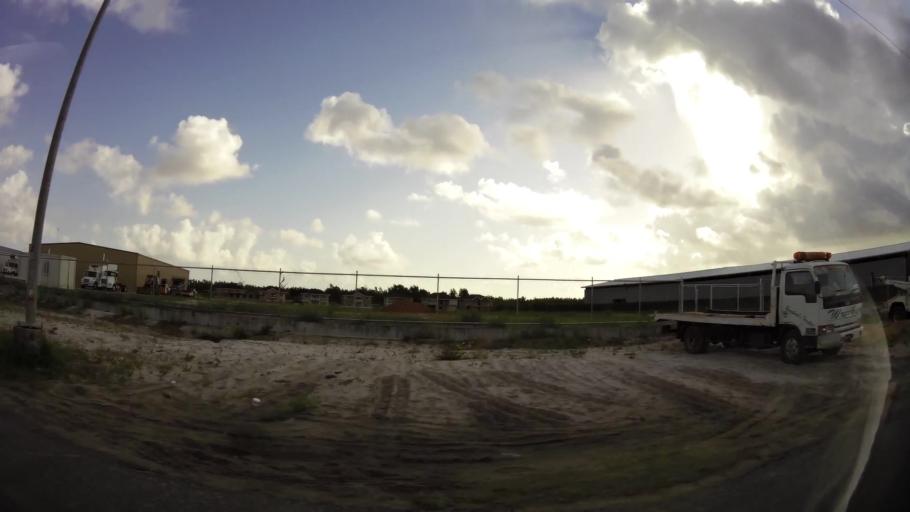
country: GY
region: Demerara-Mahaica
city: Georgetown
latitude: 6.8030
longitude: -58.0462
